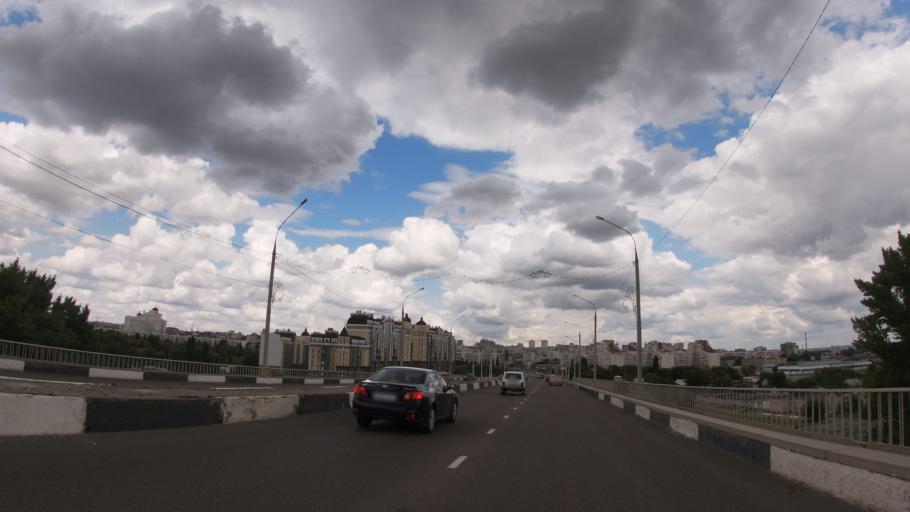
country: RU
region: Belgorod
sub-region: Belgorodskiy Rayon
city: Belgorod
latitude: 50.5860
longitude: 36.5871
